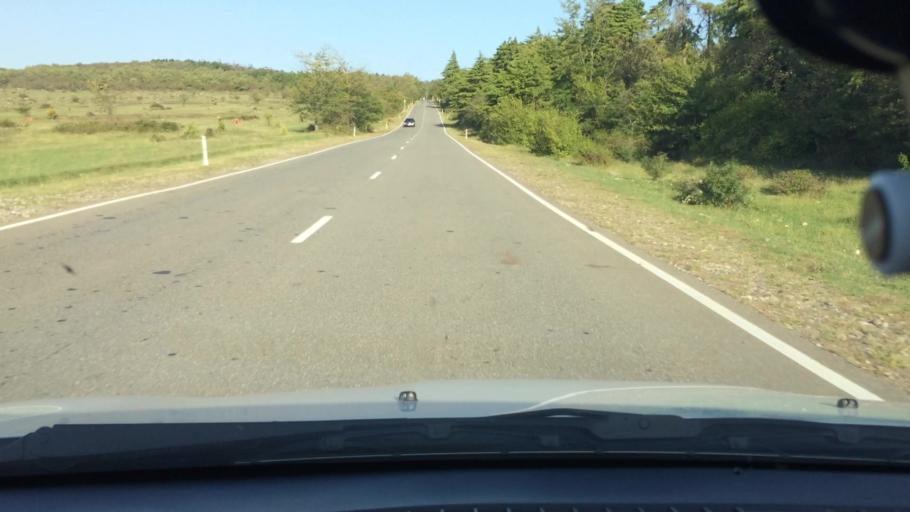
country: GE
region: Imereti
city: Kutaisi
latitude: 42.2417
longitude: 42.7638
